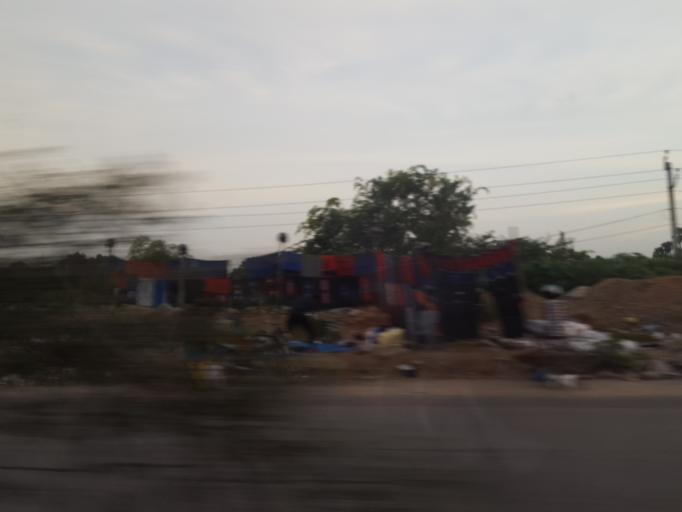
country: IN
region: Telangana
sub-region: Medak
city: Serilingampalle
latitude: 17.5157
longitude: 78.3596
